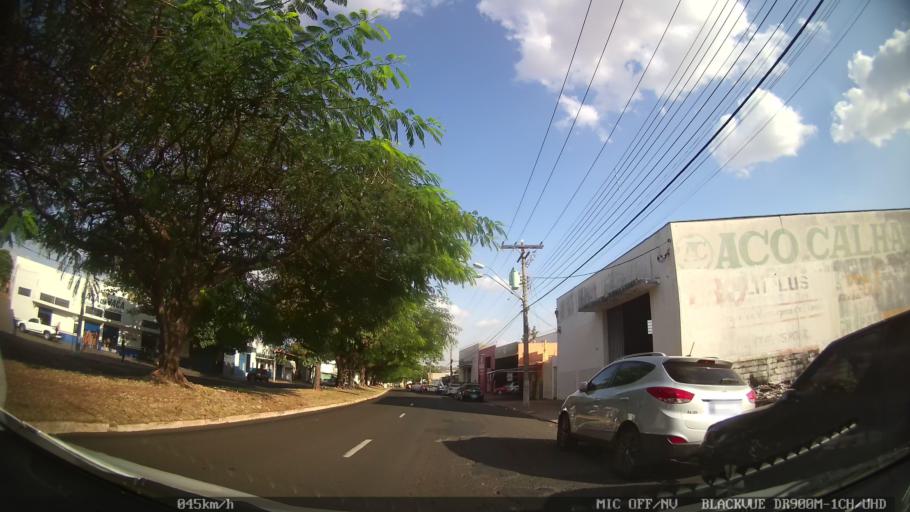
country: BR
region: Sao Paulo
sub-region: Ribeirao Preto
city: Ribeirao Preto
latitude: -21.1433
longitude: -47.7997
